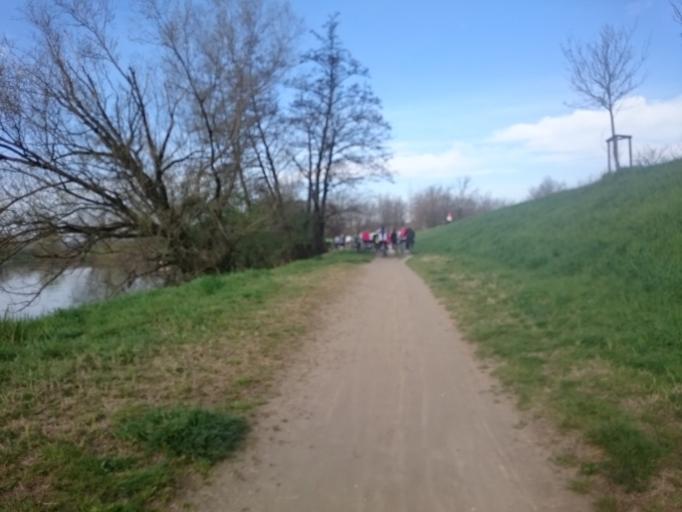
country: IT
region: Veneto
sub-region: Provincia di Padova
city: Mandriola-Sant'Agostino
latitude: 45.3923
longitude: 11.8382
